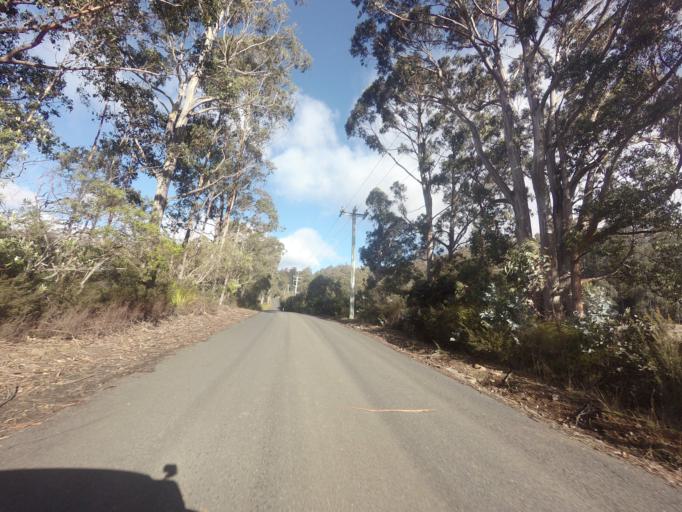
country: AU
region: Tasmania
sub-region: Glenorchy
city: Berriedale
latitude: -42.8383
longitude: 147.1585
